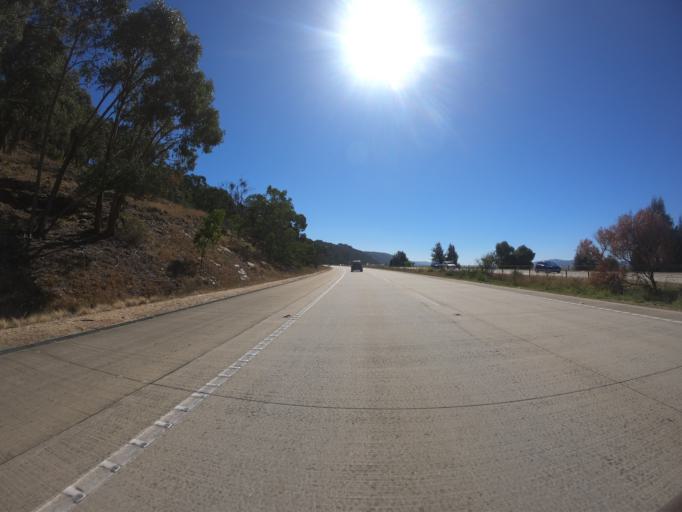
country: AU
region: New South Wales
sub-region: Yass Valley
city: Gundaroo
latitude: -35.0935
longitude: 149.3760
